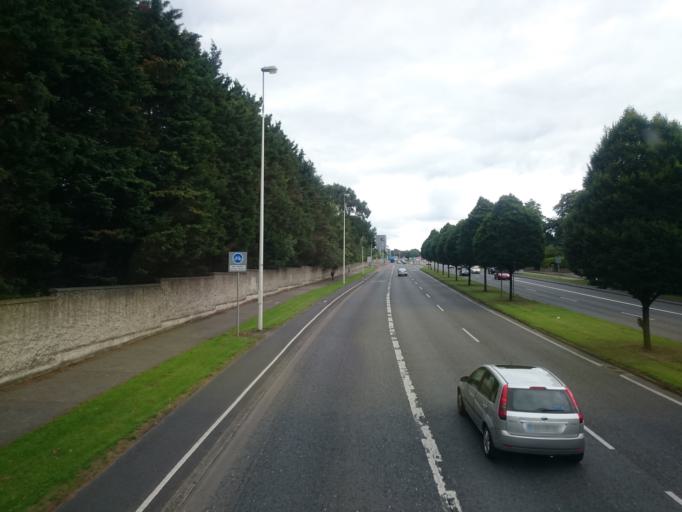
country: IE
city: Booterstown
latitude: 53.3016
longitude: -6.2063
